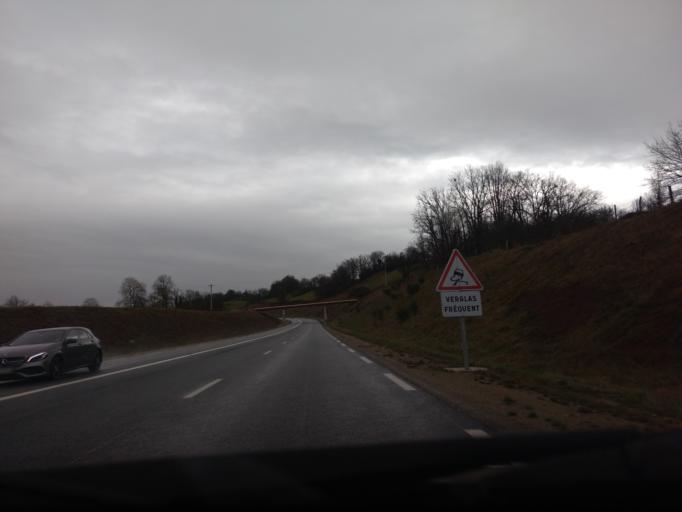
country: FR
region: Midi-Pyrenees
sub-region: Departement de l'Aveyron
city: Firmi
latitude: 44.5189
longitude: 2.3425
